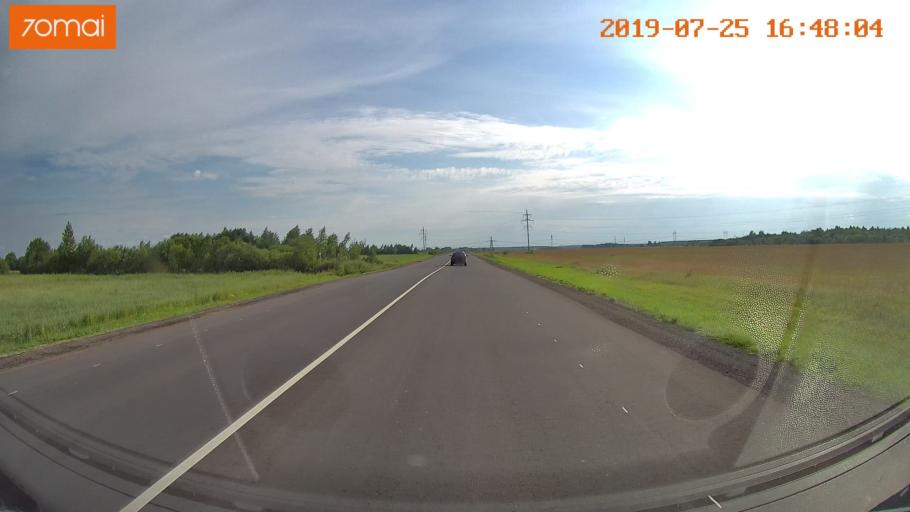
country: RU
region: Ivanovo
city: Privolzhsk
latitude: 57.3604
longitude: 41.2650
